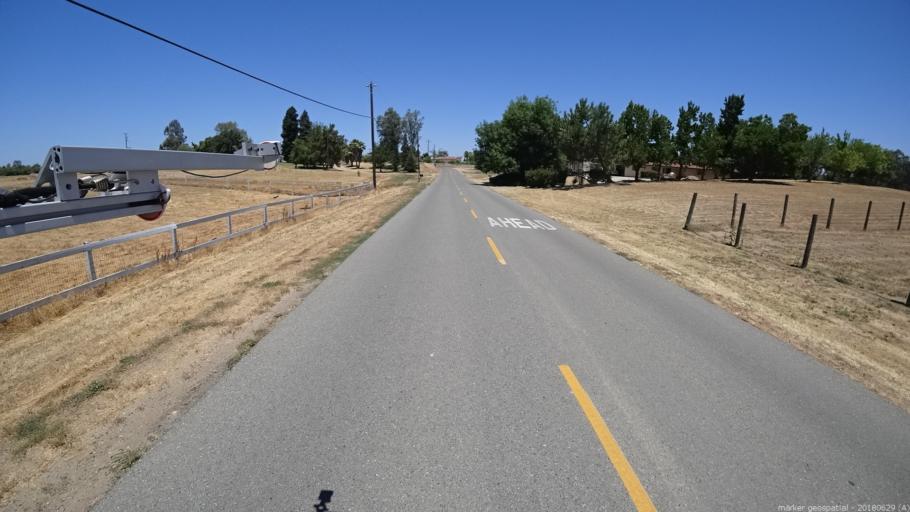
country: US
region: California
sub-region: Madera County
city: Parksdale
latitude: 36.9938
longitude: -119.9915
